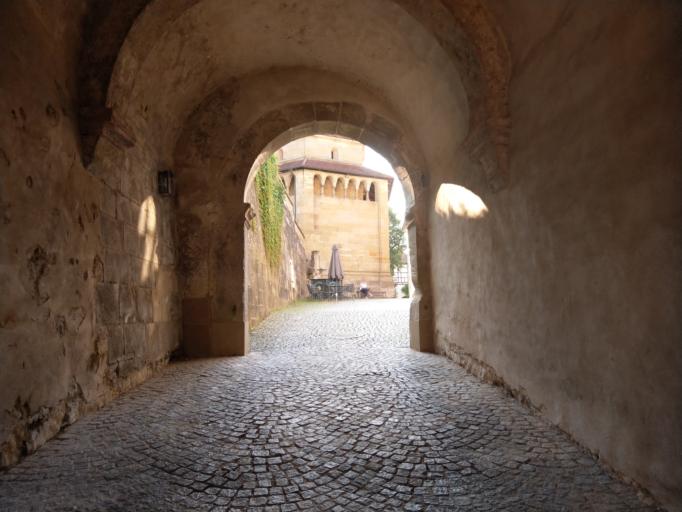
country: DE
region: Baden-Wuerttemberg
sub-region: Regierungsbezirk Stuttgart
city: Schwaebisch Hall
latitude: 49.1001
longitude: 9.7510
